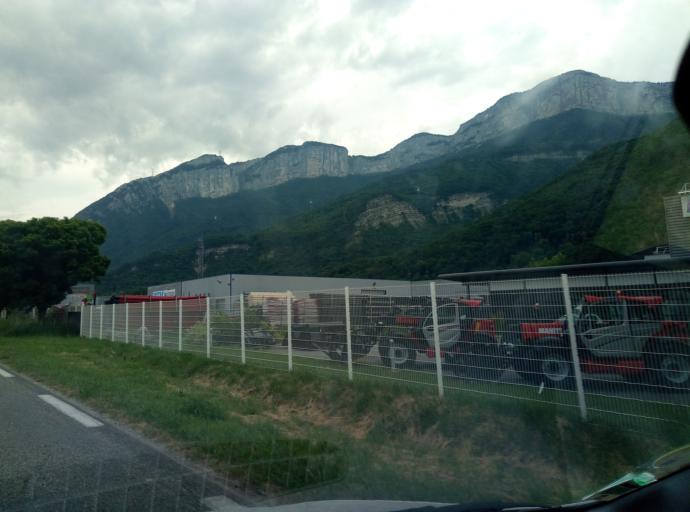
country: FR
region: Rhone-Alpes
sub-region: Departement de l'Isere
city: Noyarey
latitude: 45.2572
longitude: 5.6274
